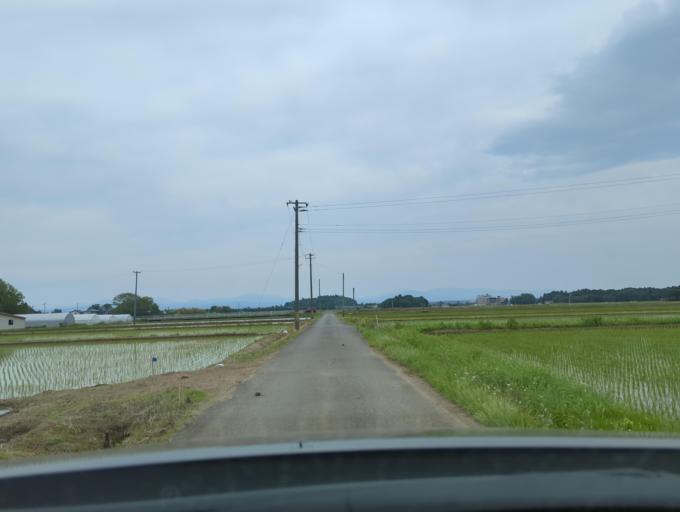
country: JP
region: Fukushima
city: Koriyama
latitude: 37.3885
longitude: 140.2995
